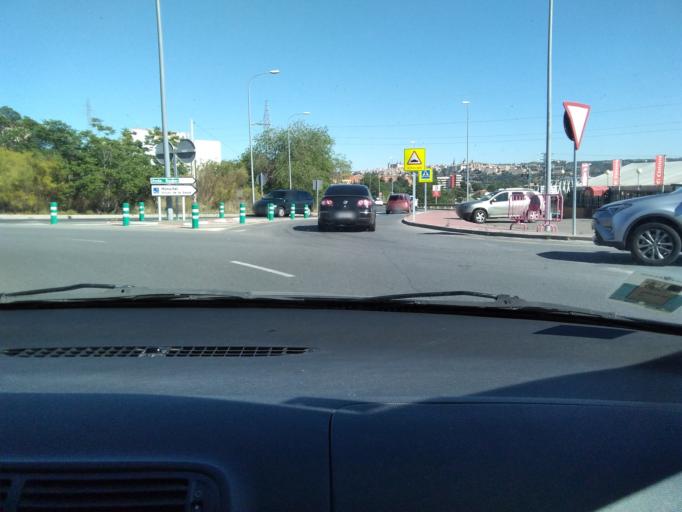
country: ES
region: Castille-La Mancha
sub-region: Province of Toledo
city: Toledo
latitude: 39.8792
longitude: -4.0477
